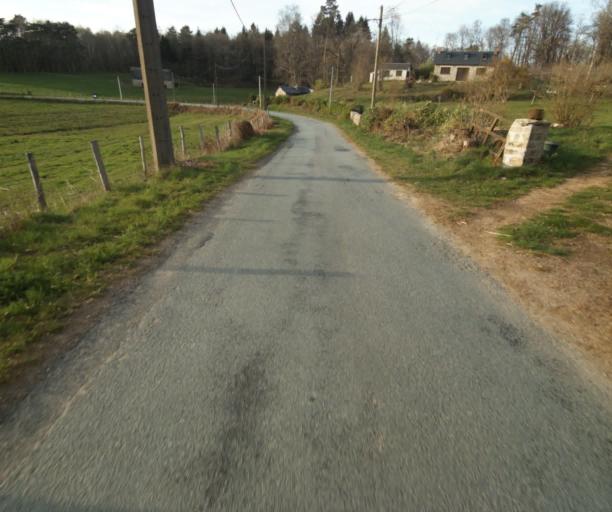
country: FR
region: Limousin
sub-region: Departement de la Correze
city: Correze
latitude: 45.3790
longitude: 1.8634
